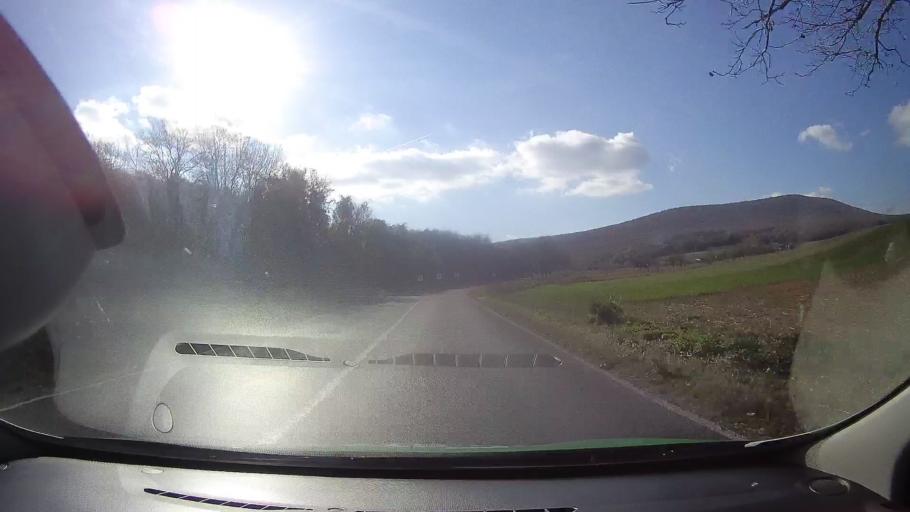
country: RO
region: Tulcea
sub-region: Oras Babadag
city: Babadag
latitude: 44.8775
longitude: 28.6915
